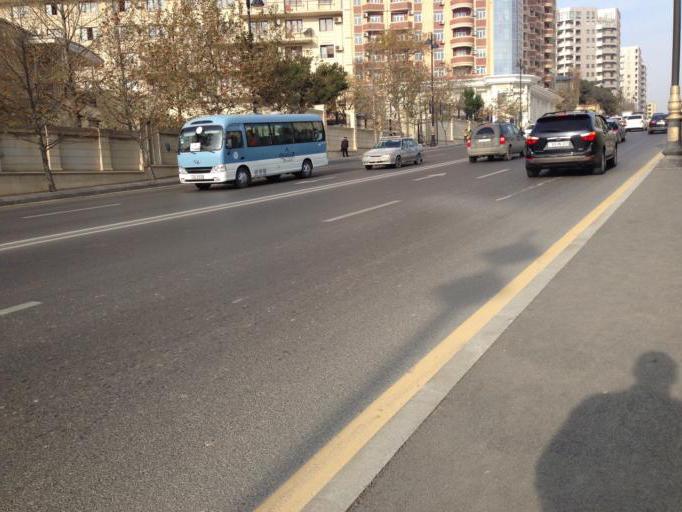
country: AZ
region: Baki
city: Baku
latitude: 40.3959
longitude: 49.8600
